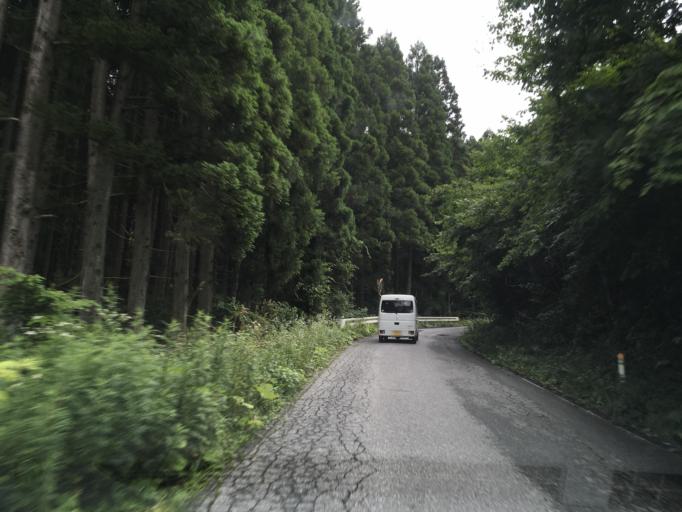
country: JP
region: Iwate
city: Ofunato
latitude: 38.8826
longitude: 141.4640
